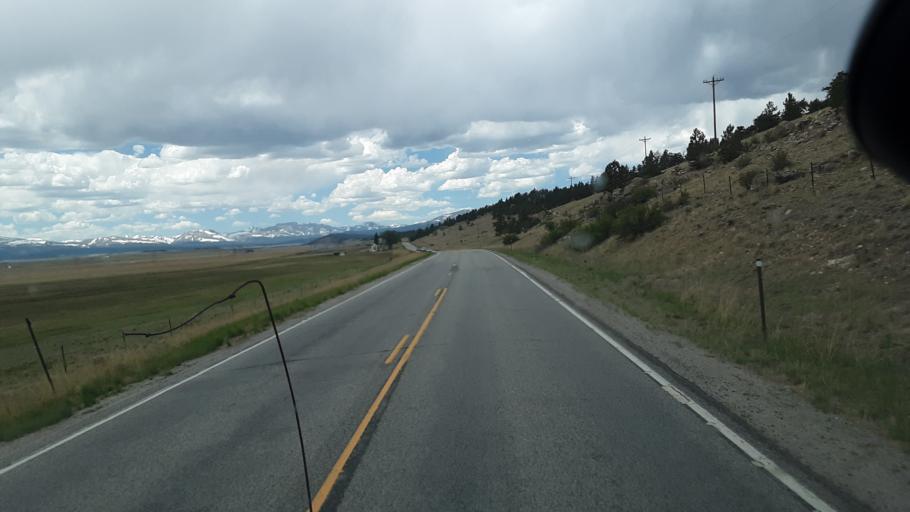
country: US
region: Colorado
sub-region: Park County
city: Fairplay
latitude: 39.0676
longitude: -105.8571
